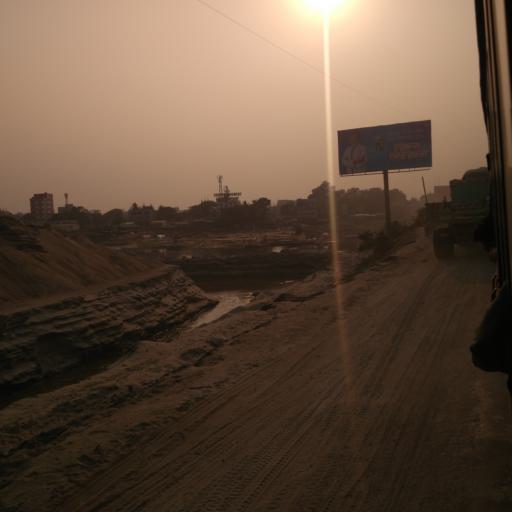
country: BD
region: Dhaka
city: Tungi
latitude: 23.8965
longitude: 90.3354
